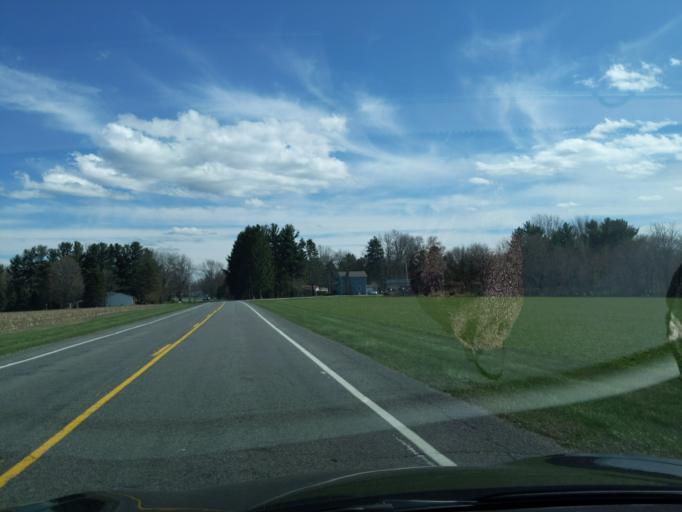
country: US
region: Michigan
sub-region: Ingham County
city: Mason
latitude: 42.5615
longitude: -84.4091
